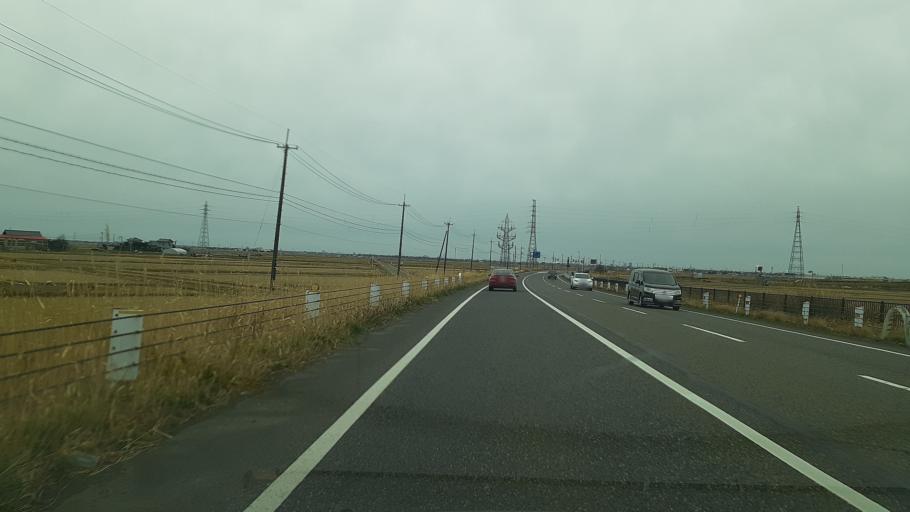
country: JP
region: Niigata
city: Niitsu-honcho
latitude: 37.7999
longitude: 139.1043
